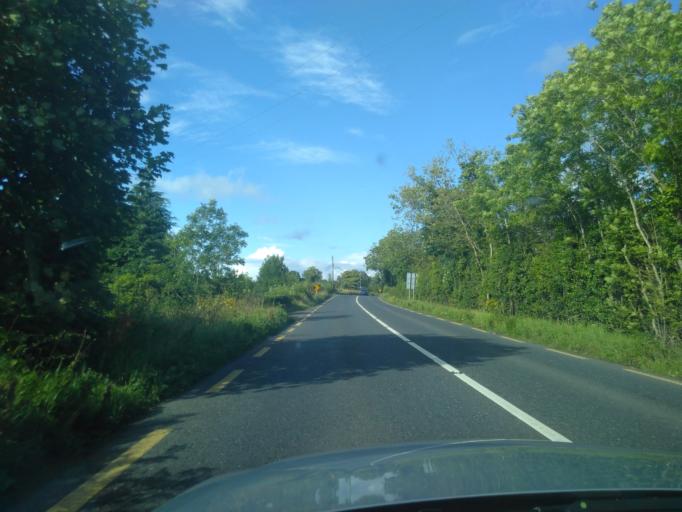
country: IE
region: Ulster
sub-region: County Donegal
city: Ballybofey
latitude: 54.8203
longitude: -7.7562
